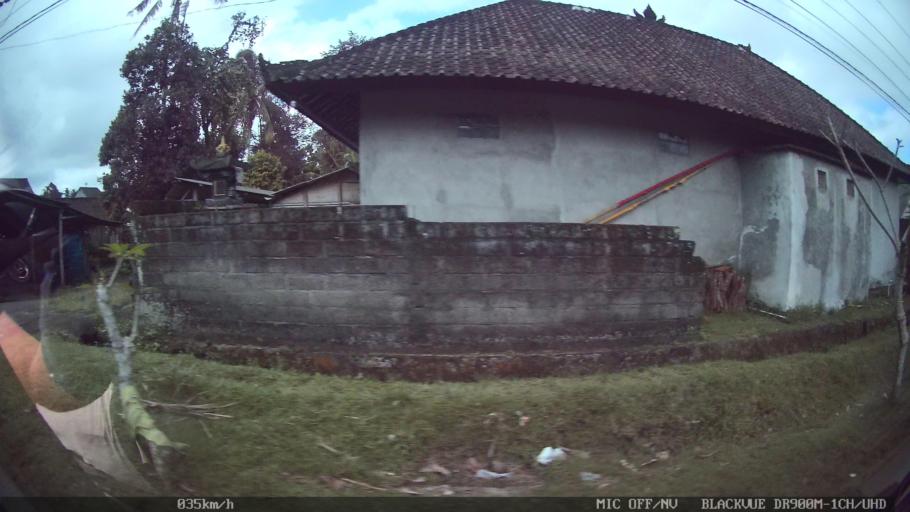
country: ID
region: Bali
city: Banjar Pesalakan
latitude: -8.4870
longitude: 115.3047
